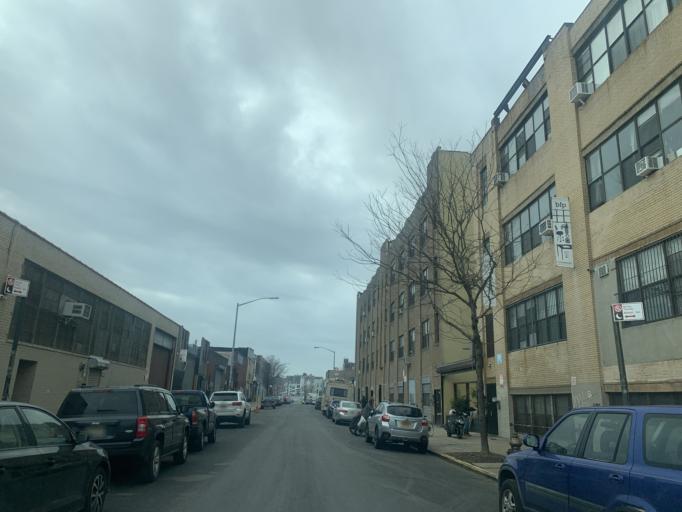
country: US
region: New York
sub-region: Queens County
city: Long Island City
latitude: 40.7076
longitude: -73.9288
